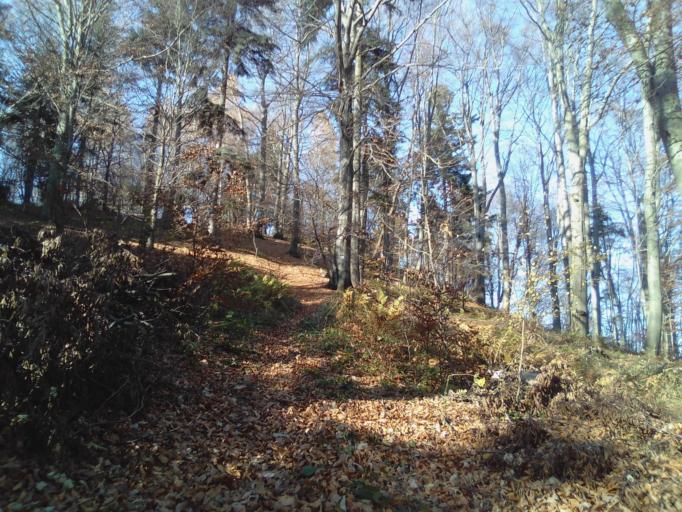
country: PL
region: Subcarpathian Voivodeship
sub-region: Powiat krosnienski
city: Leki
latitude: 49.8203
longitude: 21.6997
